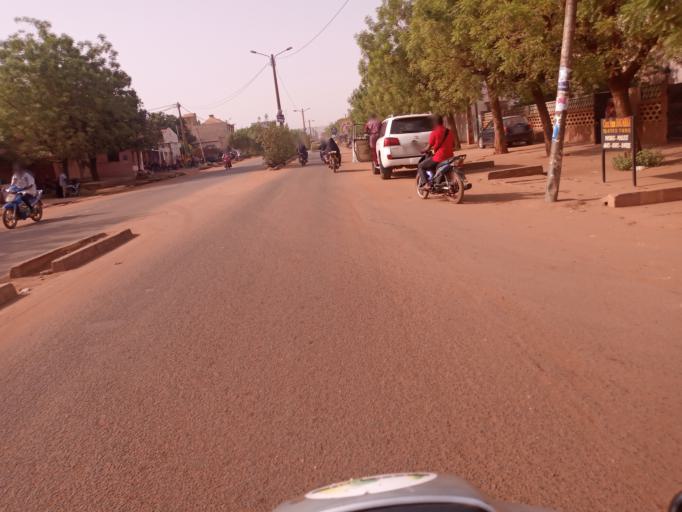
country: ML
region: Bamako
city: Bamako
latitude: 12.6654
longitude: -7.9415
